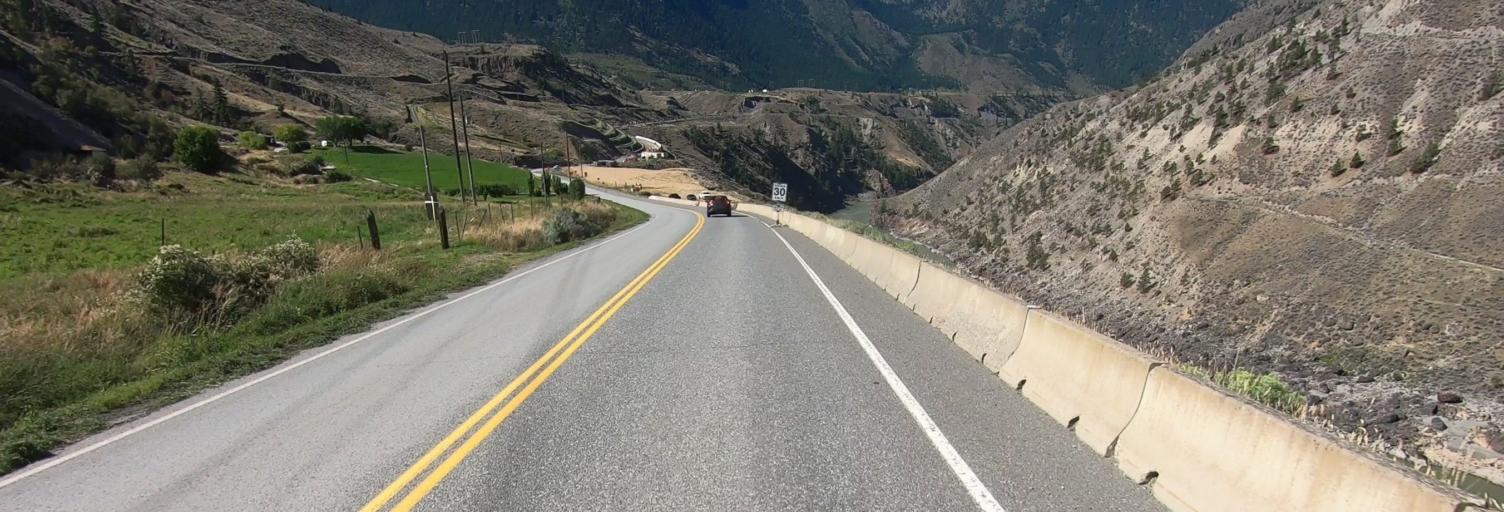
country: CA
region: British Columbia
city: Lillooet
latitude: 50.7520
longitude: -121.8429
